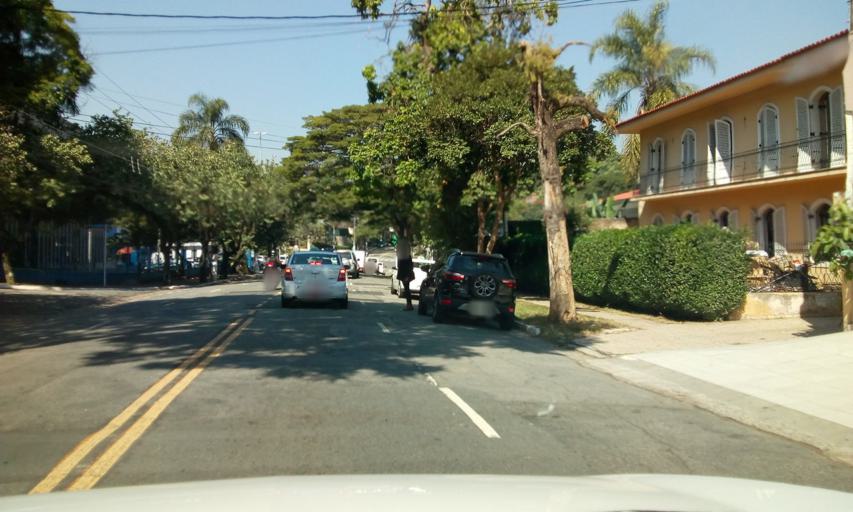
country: BR
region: Sao Paulo
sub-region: Sao Paulo
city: Sao Paulo
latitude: -23.5789
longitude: -46.7061
